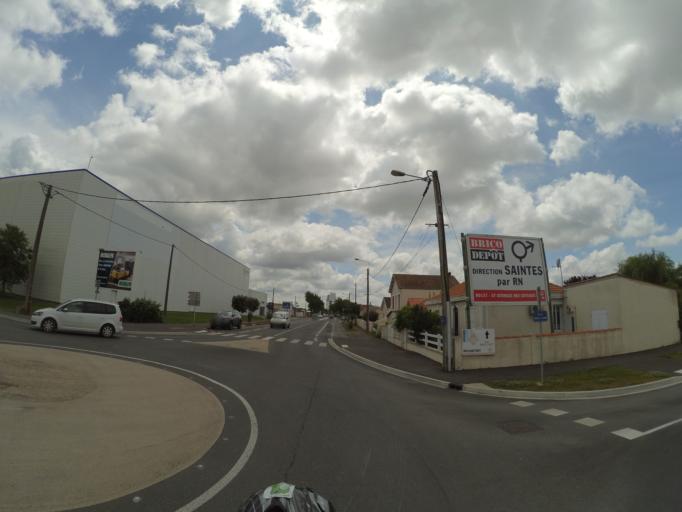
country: FR
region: Poitou-Charentes
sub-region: Departement de la Charente-Maritime
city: Rochefort
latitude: 45.9257
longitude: -0.9602
